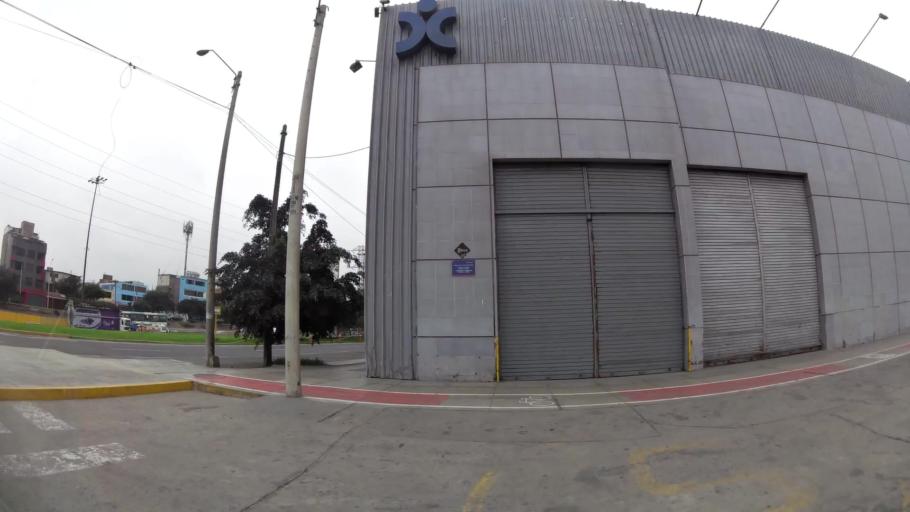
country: PE
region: Lima
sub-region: Lima
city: Surco
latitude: -12.1296
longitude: -76.9771
